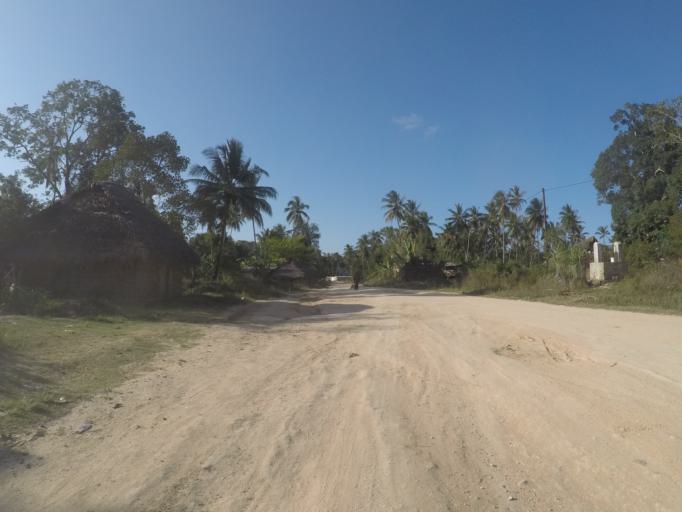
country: TZ
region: Zanzibar Central/South
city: Koani
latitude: -6.1541
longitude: 39.2875
